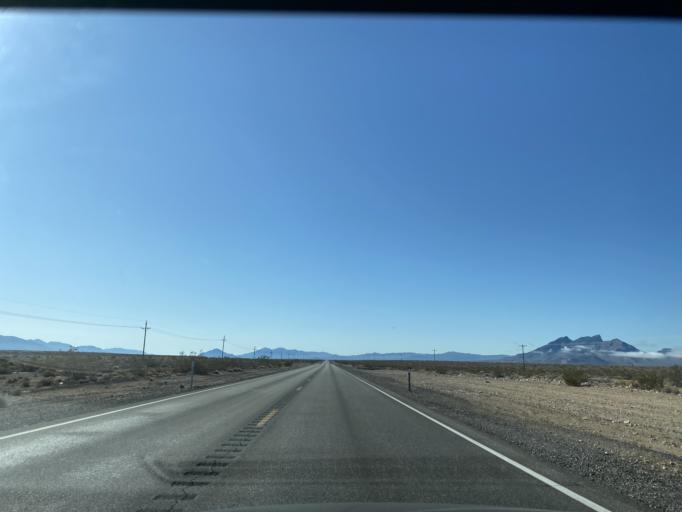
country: US
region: Nevada
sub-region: Nye County
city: Pahrump
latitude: 36.4772
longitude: -116.4216
